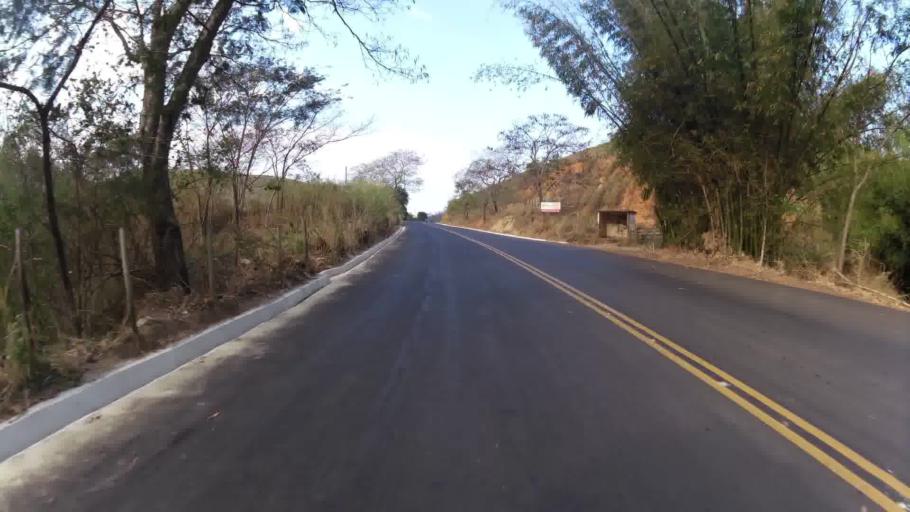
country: BR
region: Rio de Janeiro
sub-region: Santo Antonio De Padua
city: Santo Antonio de Padua
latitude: -21.4894
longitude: -42.0662
